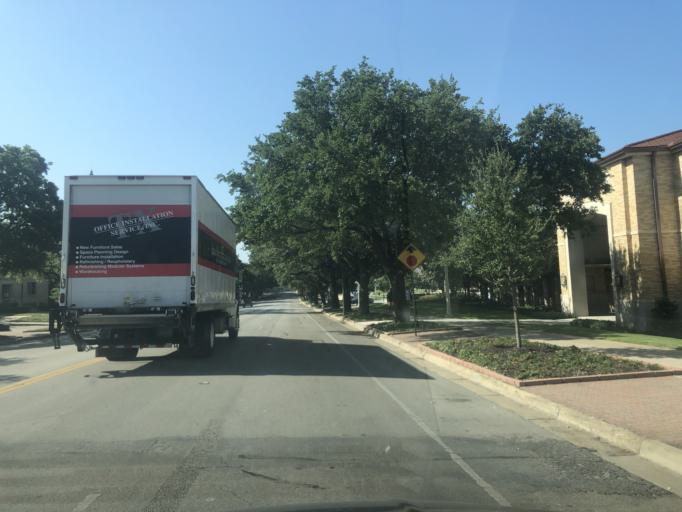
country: US
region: Texas
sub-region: Tarrant County
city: Fort Worth
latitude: 32.7111
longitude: -97.3655
